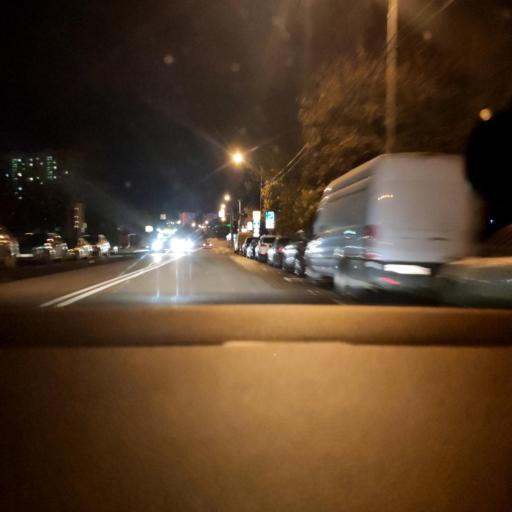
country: RU
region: Moscow
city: Orekhovo-Borisovo
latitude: 55.5968
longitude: 37.7165
